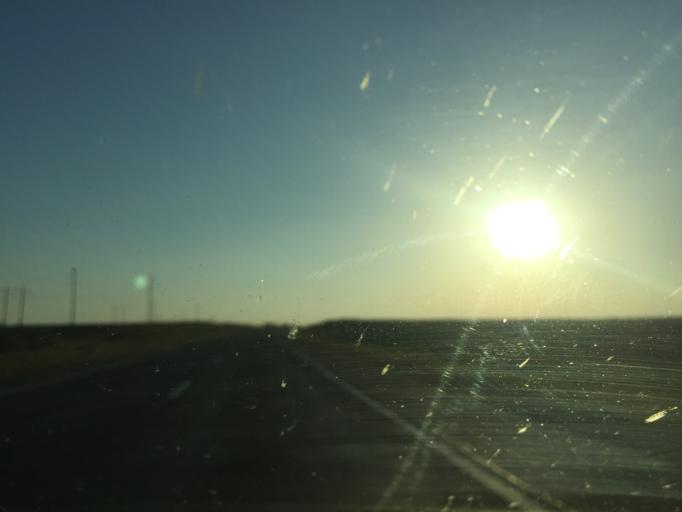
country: BY
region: Mogilev
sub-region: Mahilyowski Rayon
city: Veyno
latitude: 53.8012
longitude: 30.4444
